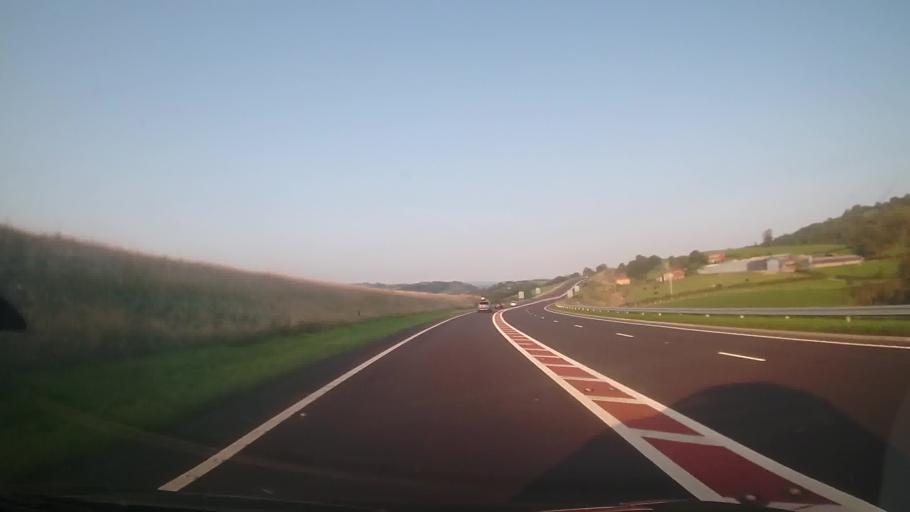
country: GB
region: Wales
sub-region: Sir Powys
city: Newtown
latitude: 52.5063
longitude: -3.3111
